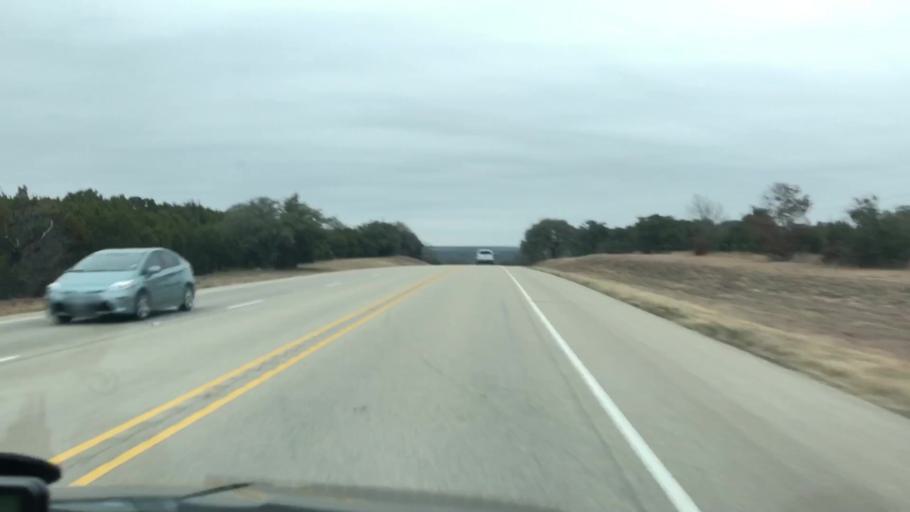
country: US
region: Texas
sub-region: Hamilton County
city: Hico
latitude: 31.9138
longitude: -98.0808
